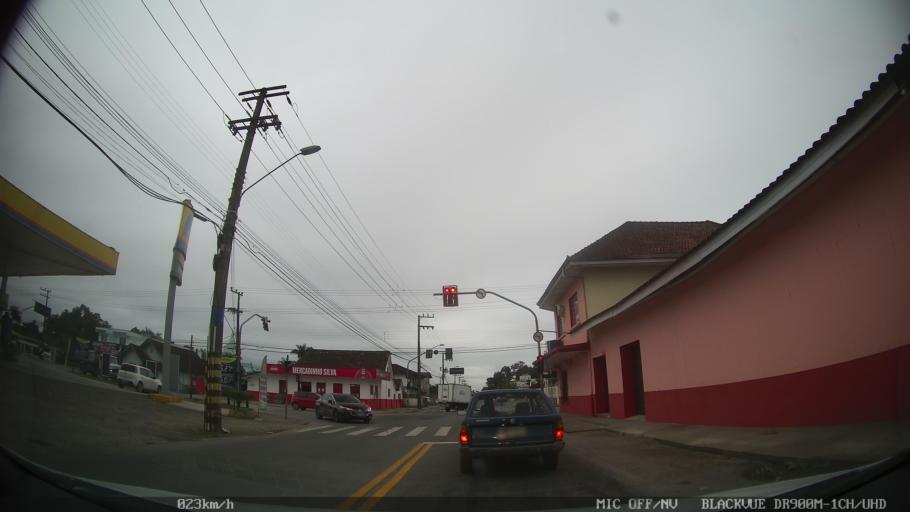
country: BR
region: Santa Catarina
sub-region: Joinville
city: Joinville
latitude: -26.2872
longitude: -48.9205
